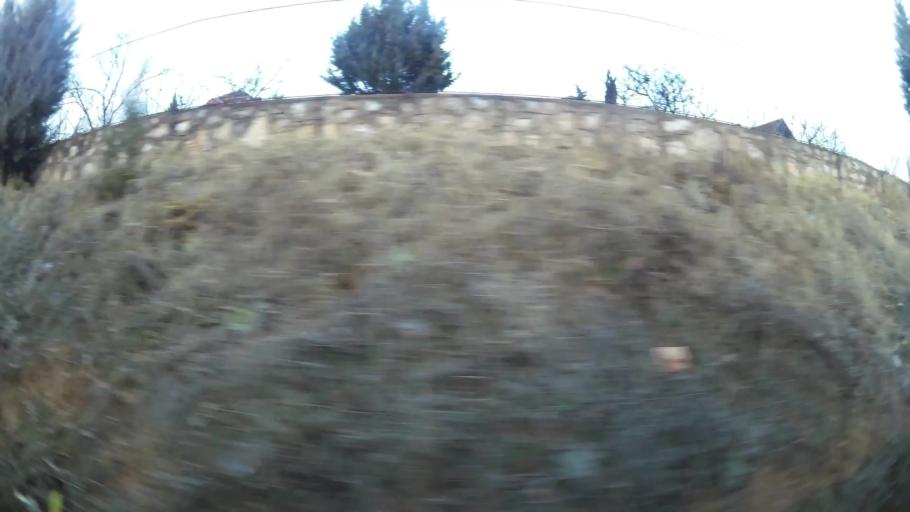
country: MK
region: Aracinovo
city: Arachinovo
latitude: 42.0315
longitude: 21.5568
